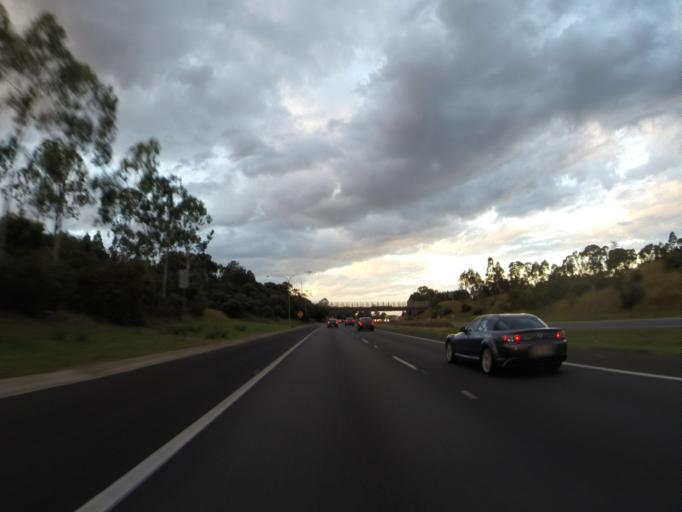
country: AU
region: New South Wales
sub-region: Campbelltown Municipality
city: Glen Alpine
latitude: -34.0628
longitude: 150.7842
